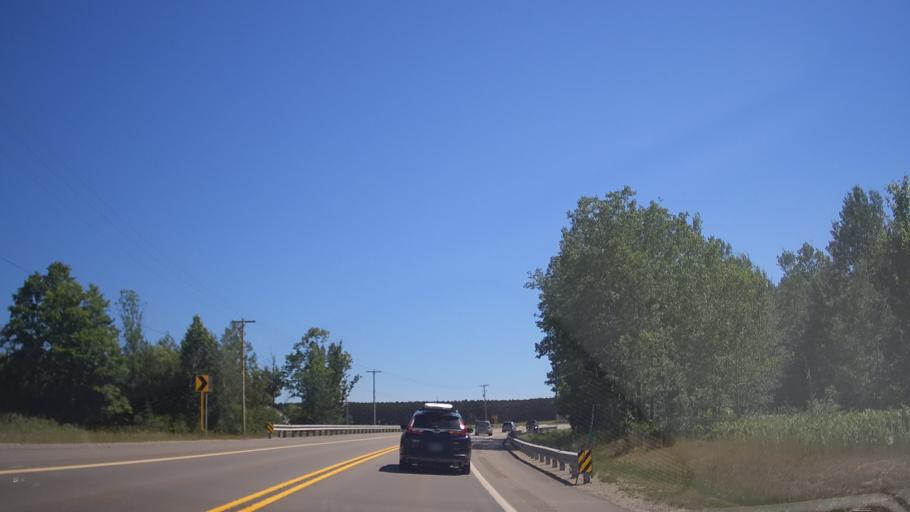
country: US
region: Michigan
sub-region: Mackinac County
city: Saint Ignace
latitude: 45.6178
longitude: -84.7800
